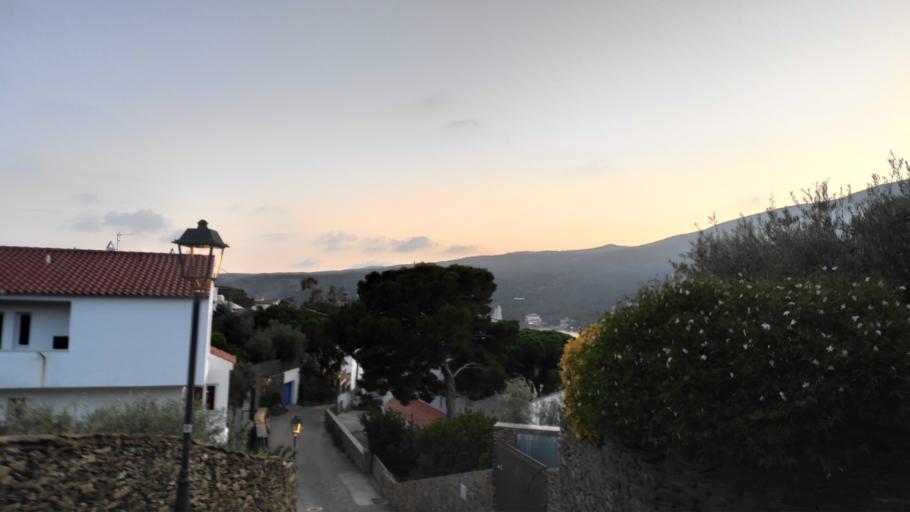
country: ES
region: Catalonia
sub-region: Provincia de Girona
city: Cadaques
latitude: 42.2903
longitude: 3.2823
